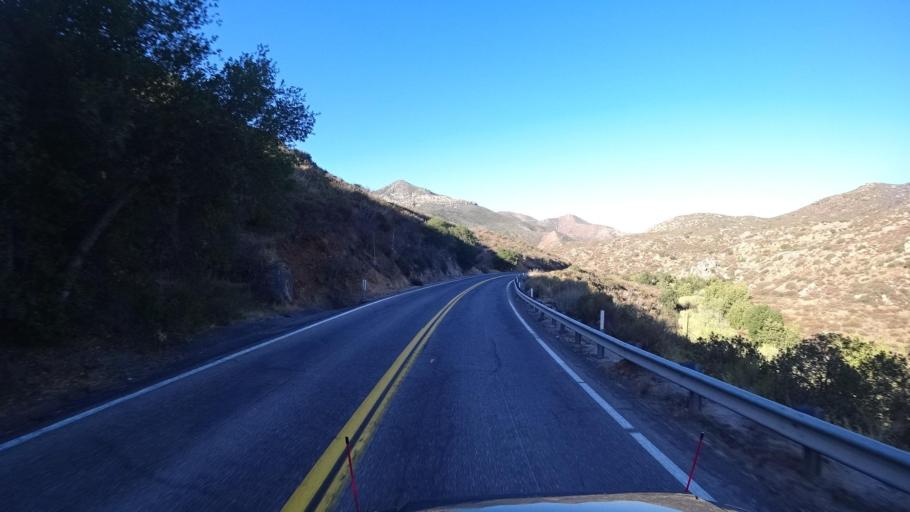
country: MX
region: Baja California
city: Tecate
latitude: 32.5969
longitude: -116.6567
